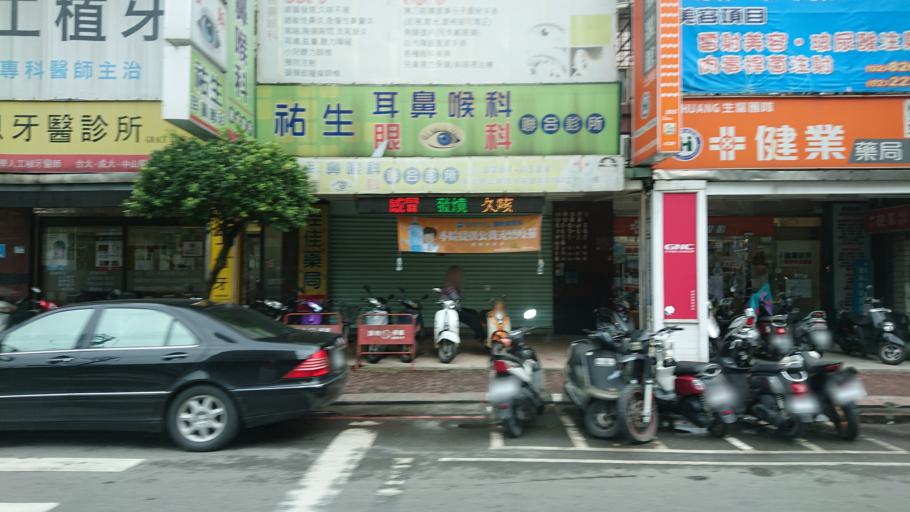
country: TW
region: Taipei
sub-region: Taipei
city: Banqiao
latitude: 24.9732
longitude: 121.4406
